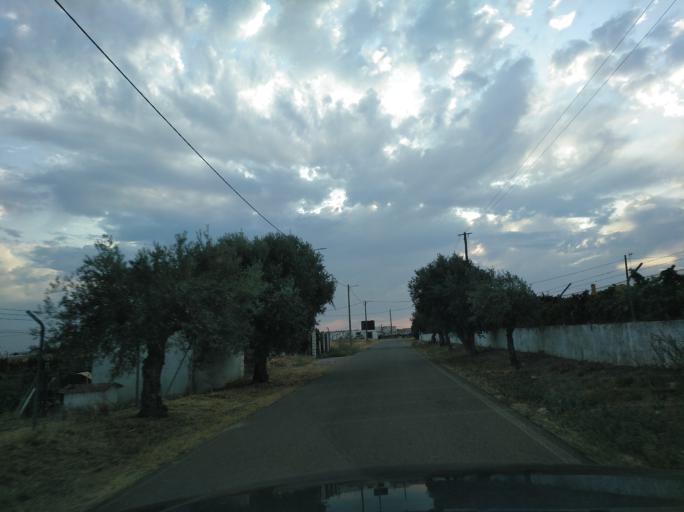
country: PT
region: Portalegre
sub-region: Campo Maior
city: Campo Maior
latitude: 39.0174
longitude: -7.0524
